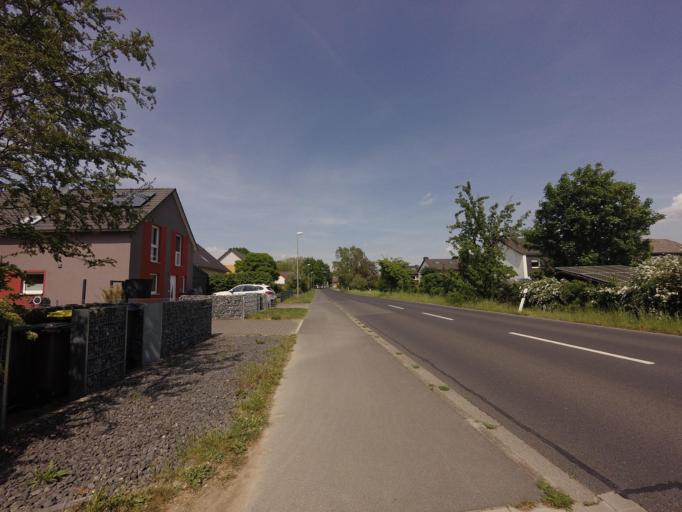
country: DE
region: Lower Saxony
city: Cremlingen
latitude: 52.2883
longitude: 10.6018
